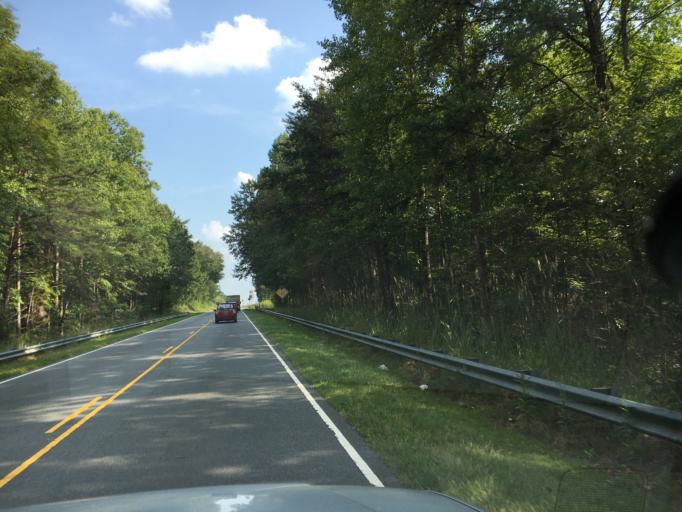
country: US
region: North Carolina
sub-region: Rutherford County
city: Rutherfordton
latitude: 35.4113
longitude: -81.9713
